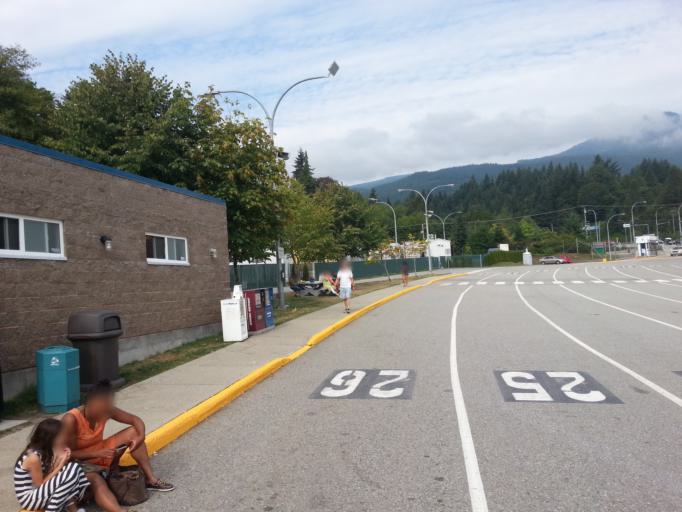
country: CA
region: British Columbia
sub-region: Sunshine Coast Regional District
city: Gibsons
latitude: 49.4330
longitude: -123.4773
